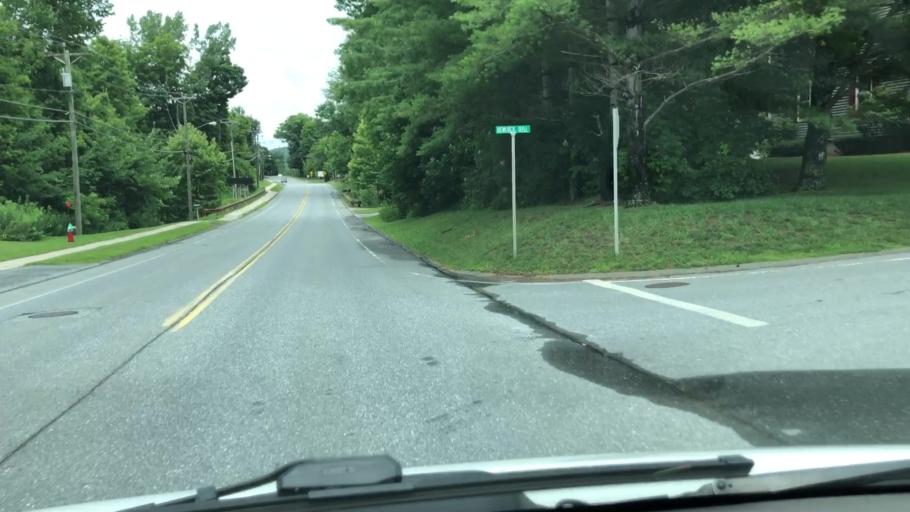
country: US
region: Massachusetts
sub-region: Berkshire County
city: Dalton
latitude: 42.4580
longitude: -73.1822
